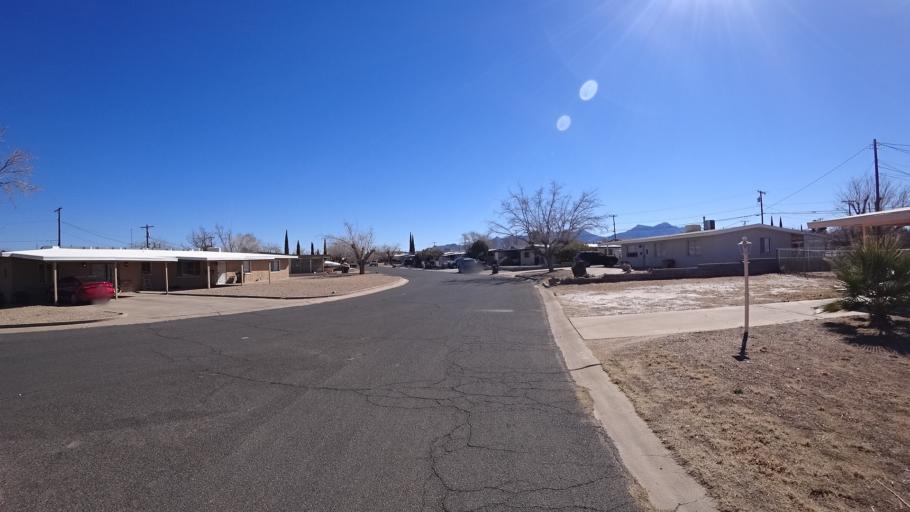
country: US
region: Arizona
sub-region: Mohave County
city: Kingman
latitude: 35.2111
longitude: -114.0234
